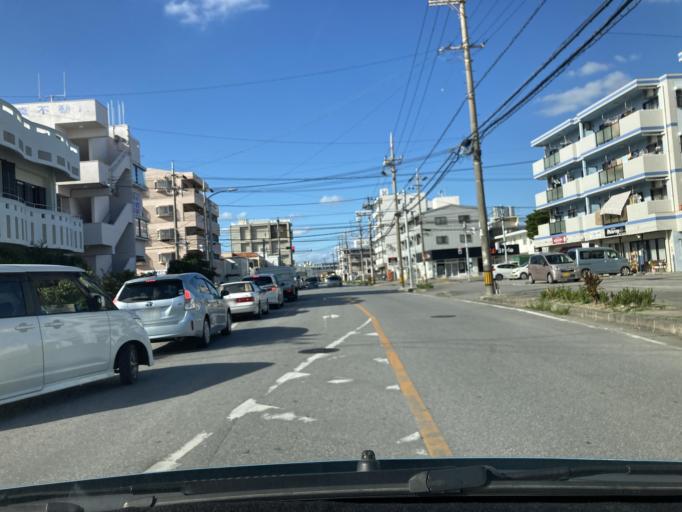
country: JP
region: Okinawa
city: Okinawa
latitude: 26.3419
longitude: 127.8241
